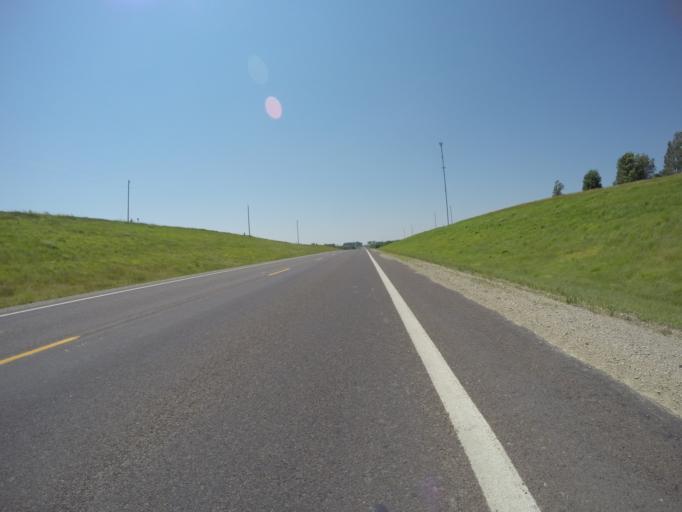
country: US
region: Kansas
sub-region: Doniphan County
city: Highland
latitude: 39.8491
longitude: -95.2652
